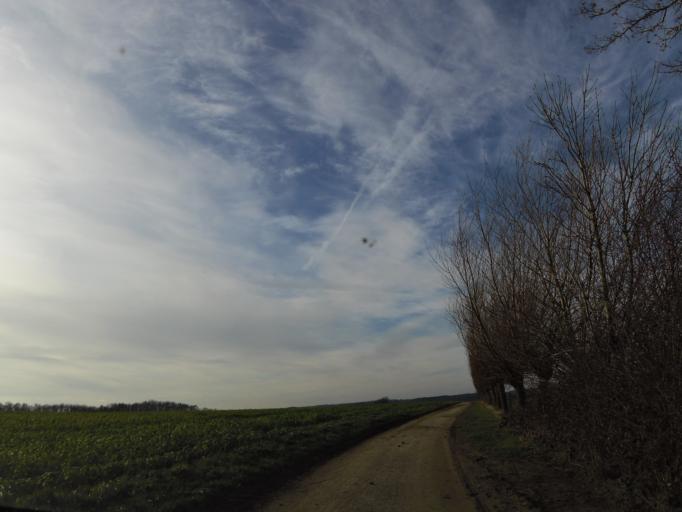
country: NL
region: Limburg
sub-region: Gemeente Voerendaal
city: Ubachsberg
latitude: 50.8348
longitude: 5.9184
